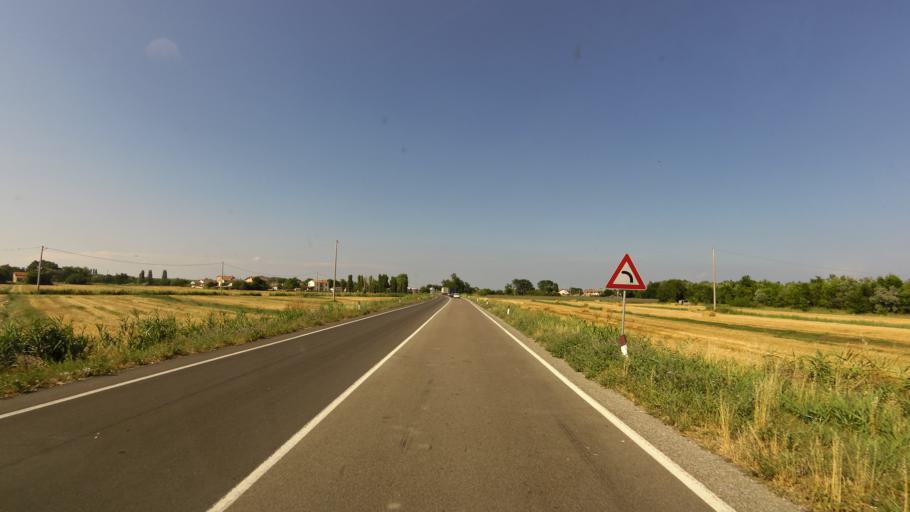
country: IT
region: Emilia-Romagna
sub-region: Provincia di Ravenna
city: Marina Romea
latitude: 44.5592
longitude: 12.2474
